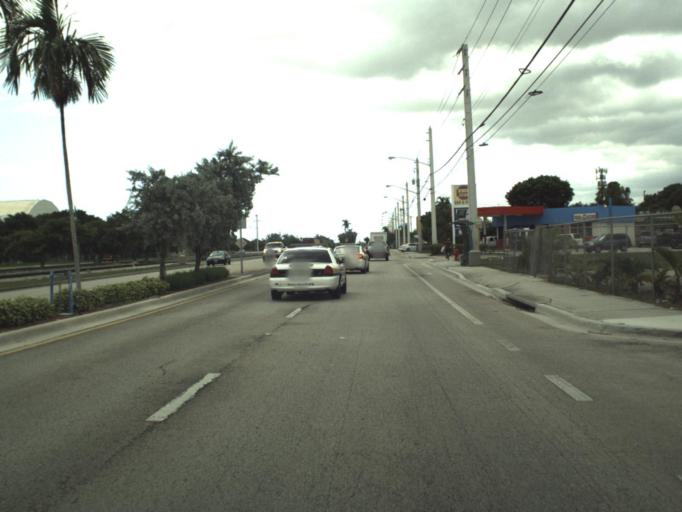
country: US
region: Florida
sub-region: Broward County
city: Kendall Green
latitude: 26.2535
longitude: -80.1200
